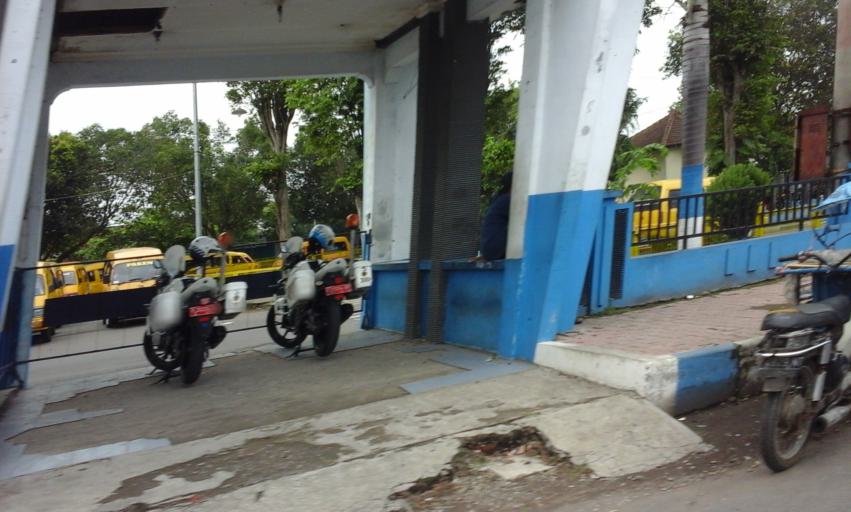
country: ID
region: East Java
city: Jubung
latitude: -8.1980
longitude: 113.6312
